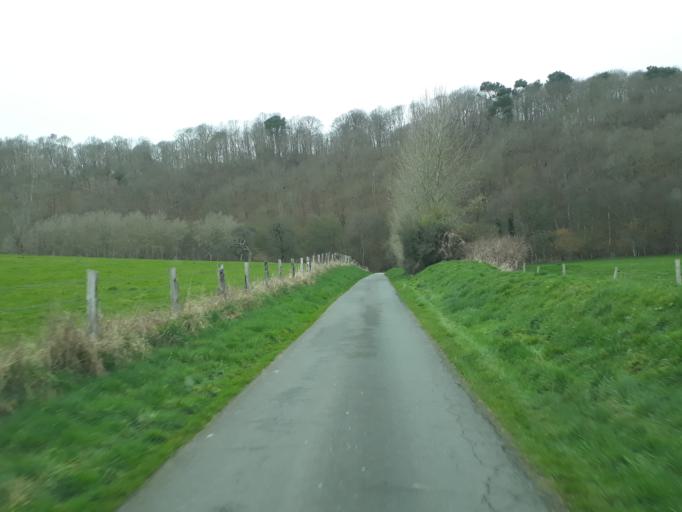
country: FR
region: Haute-Normandie
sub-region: Departement de la Seine-Maritime
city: Les Loges
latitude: 49.6747
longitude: 0.2647
